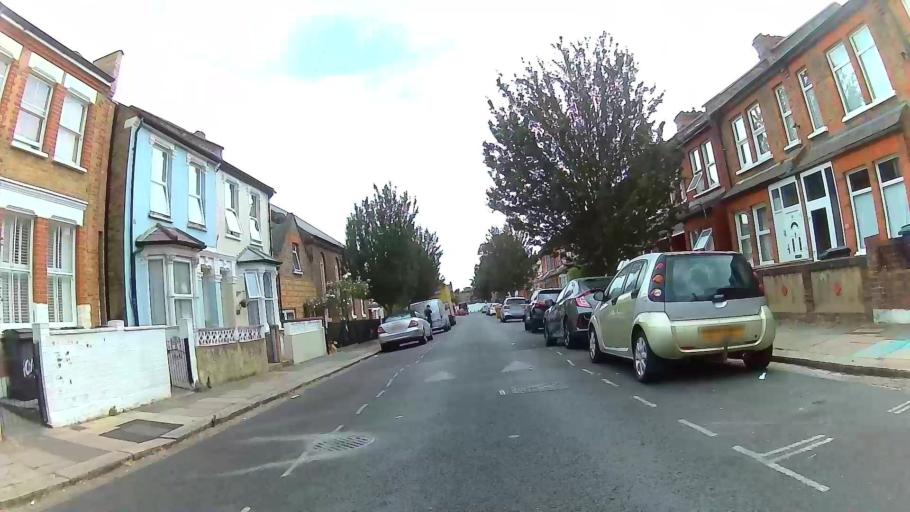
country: GB
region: England
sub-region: Greater London
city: Harringay
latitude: 51.5910
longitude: -0.0767
